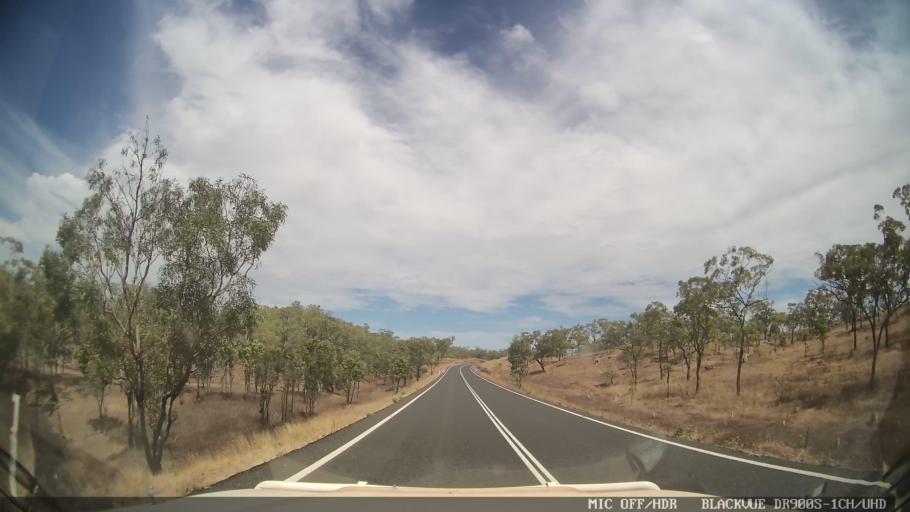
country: AU
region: Queensland
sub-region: Cairns
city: Port Douglas
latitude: -16.1466
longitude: 144.7675
